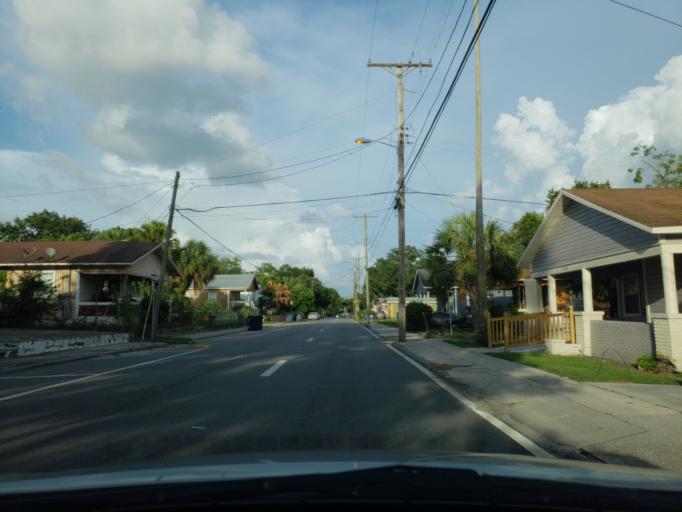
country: US
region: Florida
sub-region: Hillsborough County
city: Tampa
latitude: 27.9668
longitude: -82.4302
